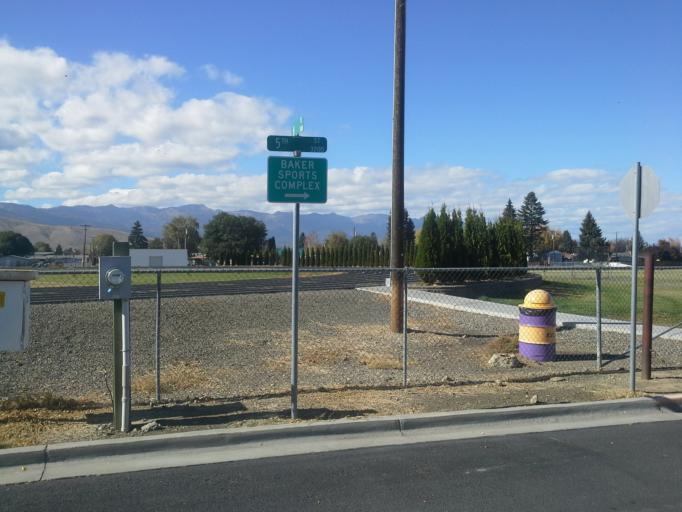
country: US
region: Oregon
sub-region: Baker County
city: Baker City
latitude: 44.7890
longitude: -117.8358
